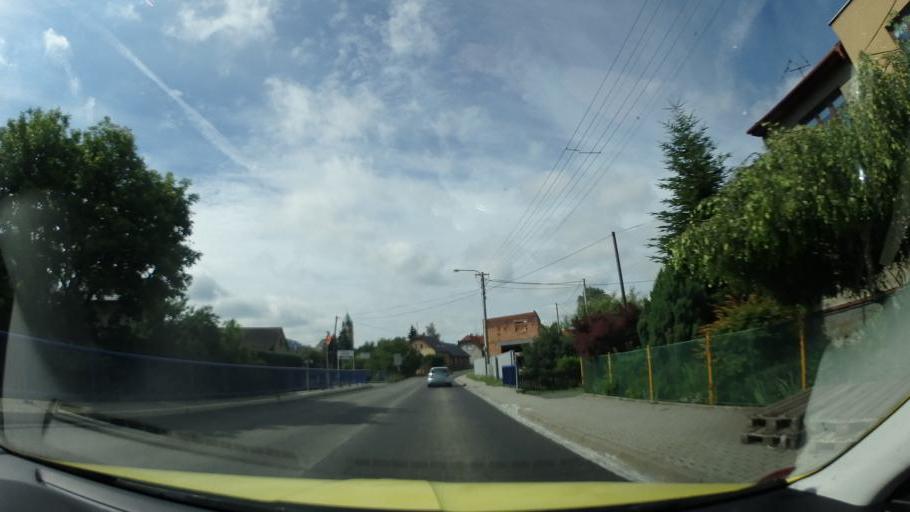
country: CZ
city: Hodslavice
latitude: 49.5408
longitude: 18.0254
